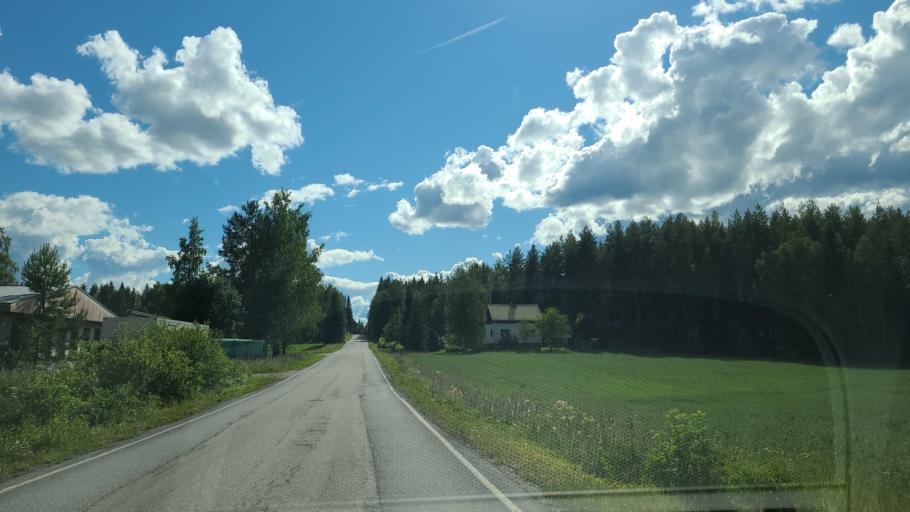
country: FI
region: Central Finland
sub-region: Jaemsae
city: Jaemsae
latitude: 61.8828
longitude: 25.2323
